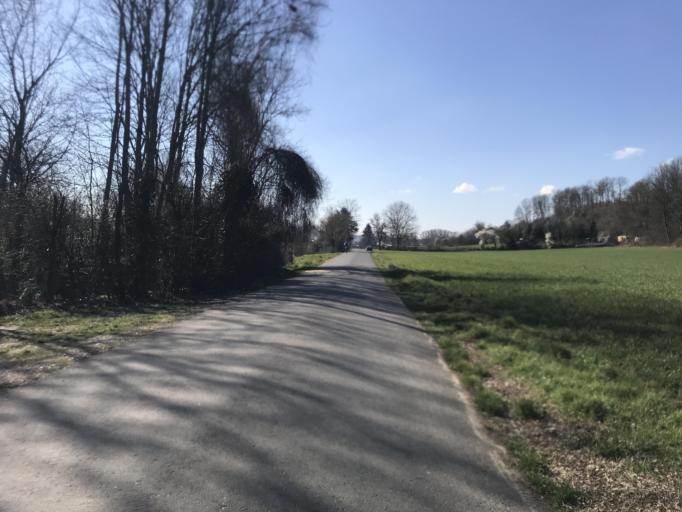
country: DE
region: Hesse
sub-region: Regierungsbezirk Darmstadt
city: Florsheim
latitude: 50.0091
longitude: 8.4069
